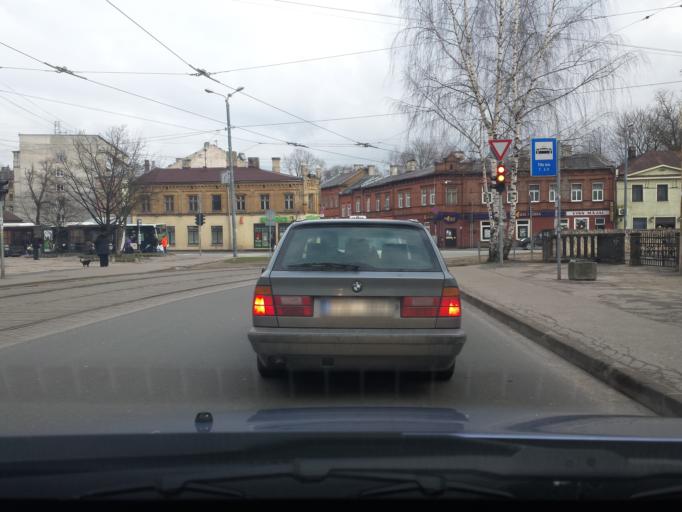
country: LV
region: Riga
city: Riga
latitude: 56.9952
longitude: 24.1261
